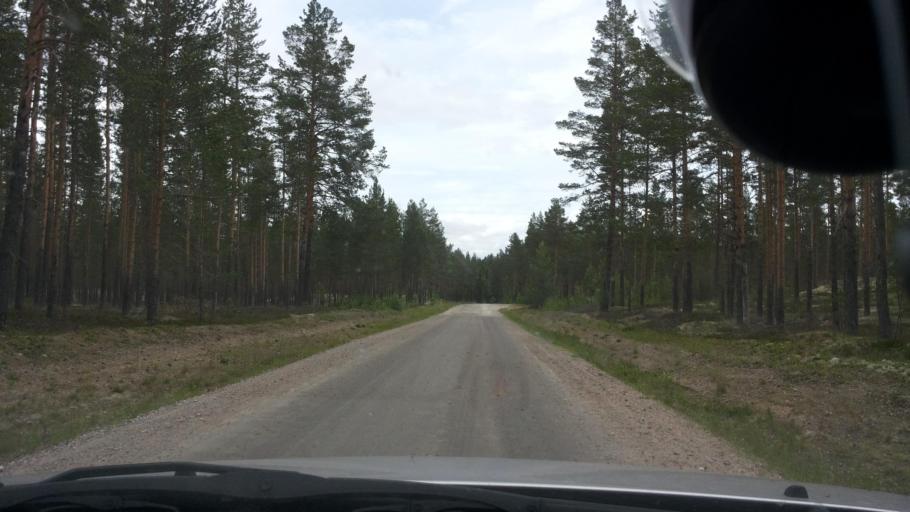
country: SE
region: Gaevleborg
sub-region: Ovanakers Kommun
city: Edsbyn
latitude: 61.5119
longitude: 15.3418
